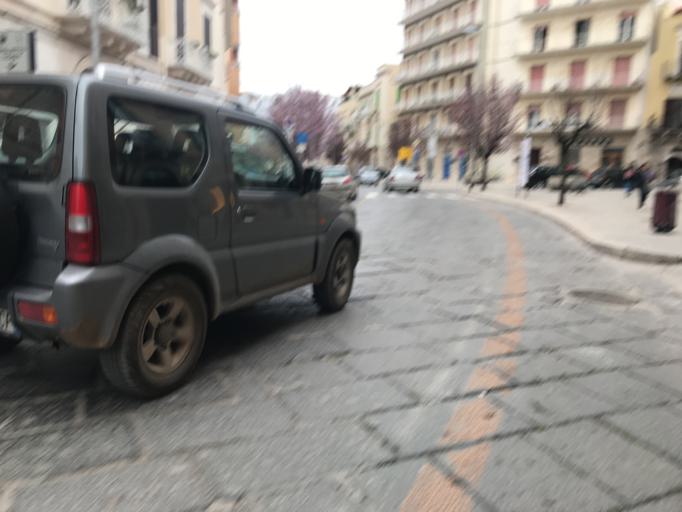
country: IT
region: Apulia
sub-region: Provincia di Bari
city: Corato
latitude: 41.1529
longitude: 16.4092
